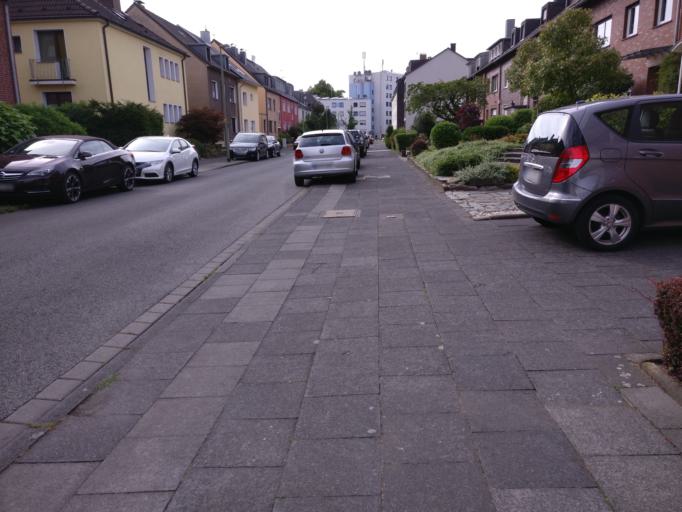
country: DE
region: North Rhine-Westphalia
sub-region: Regierungsbezirk Dusseldorf
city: Duisburg
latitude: 51.4208
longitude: 6.7929
